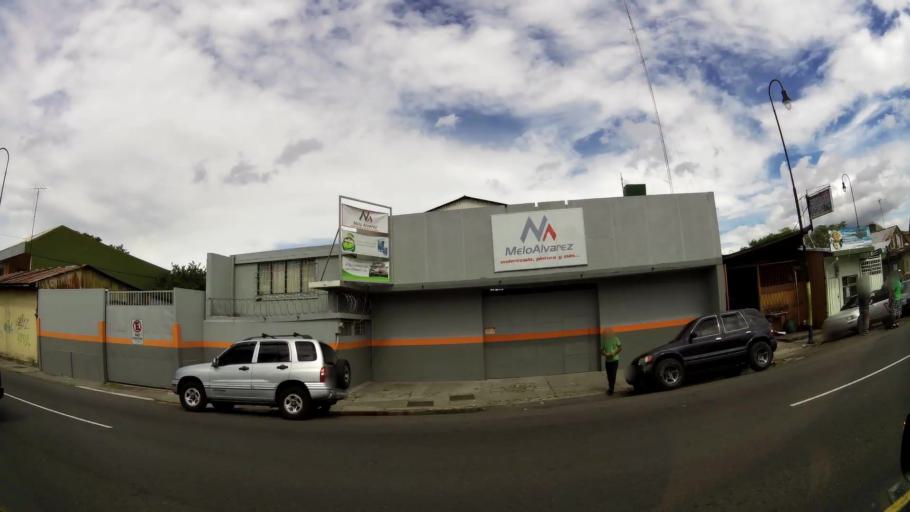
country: CR
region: San Jose
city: San Jose
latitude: 9.9246
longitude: -84.0729
